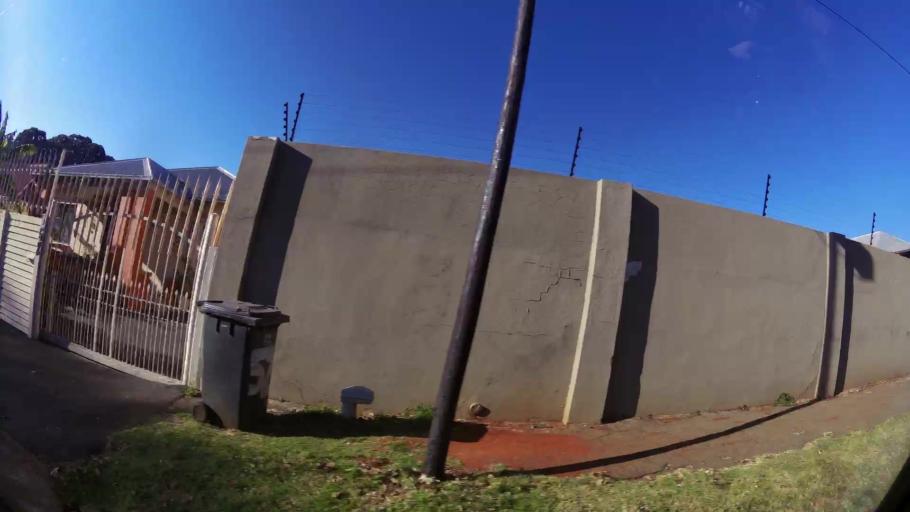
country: ZA
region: Gauteng
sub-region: City of Johannesburg Metropolitan Municipality
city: Johannesburg
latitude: -26.1909
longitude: 28.0951
